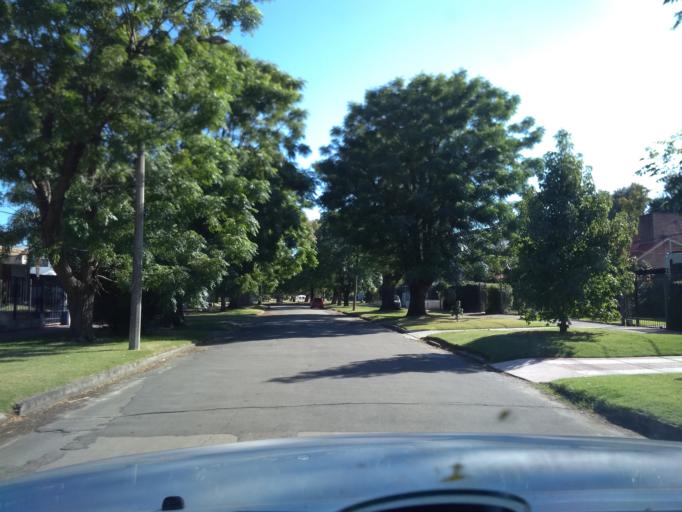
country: UY
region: Canelones
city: Paso de Carrasco
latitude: -34.8938
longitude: -56.0719
